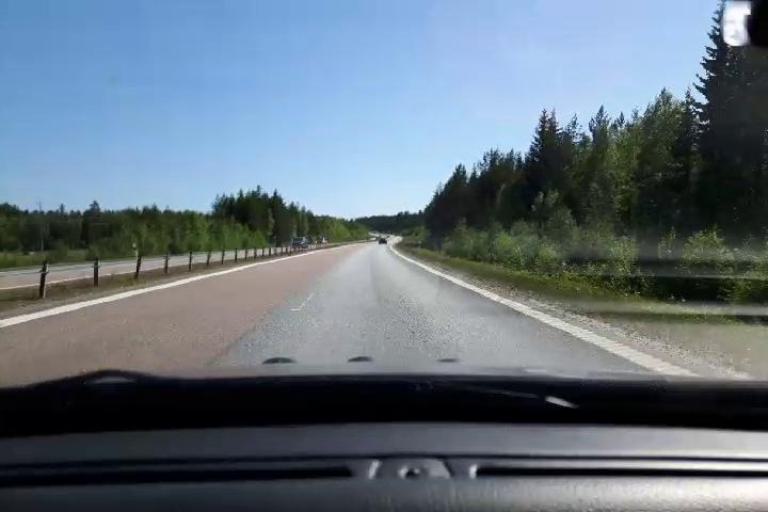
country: SE
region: Gaevleborg
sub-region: Soderhamns Kommun
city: Soderhamn
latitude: 61.4043
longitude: 16.9937
